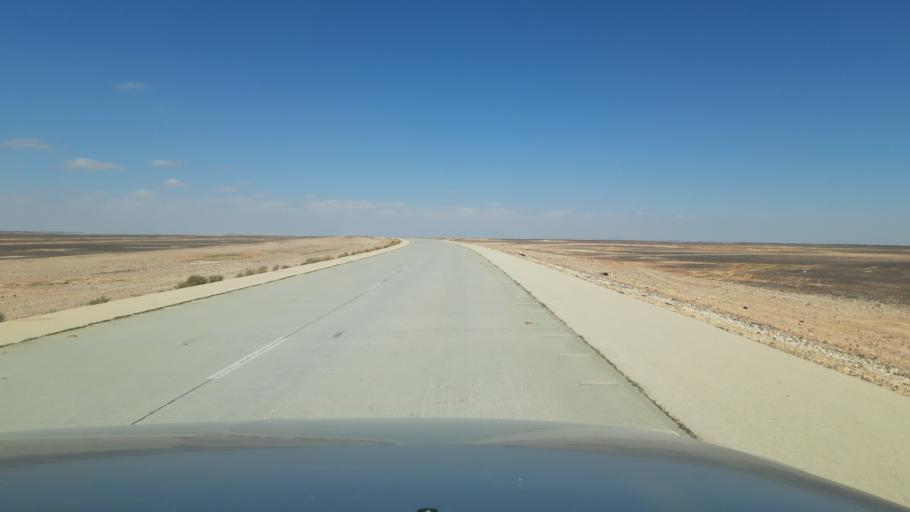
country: JO
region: Amman
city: Al Azraq ash Shamali
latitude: 31.4700
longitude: 36.8056
